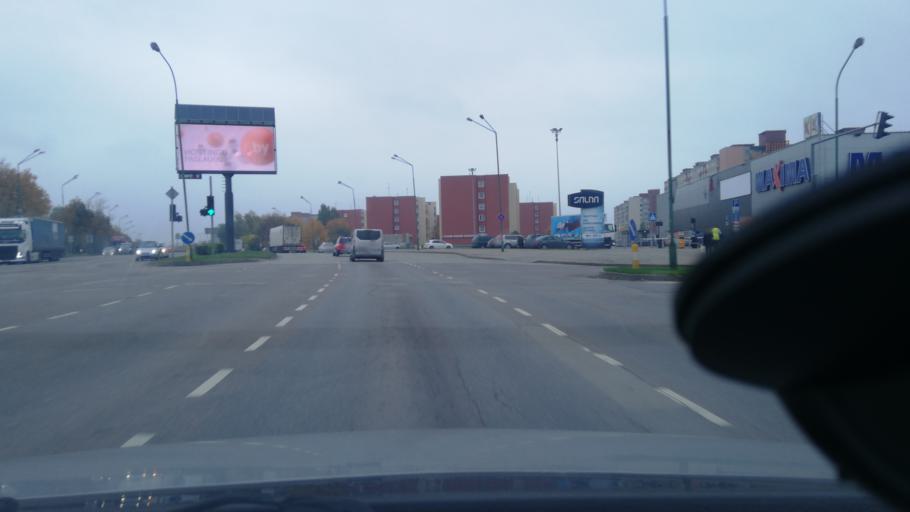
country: LT
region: Klaipedos apskritis
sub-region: Klaipeda
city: Klaipeda
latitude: 55.6777
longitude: 21.1888
